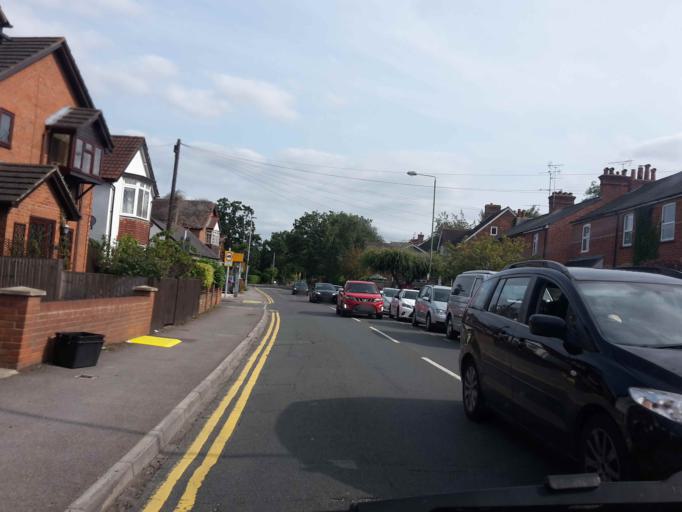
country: GB
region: England
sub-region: Wokingham
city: Wokingham
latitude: 51.4098
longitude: -0.8285
